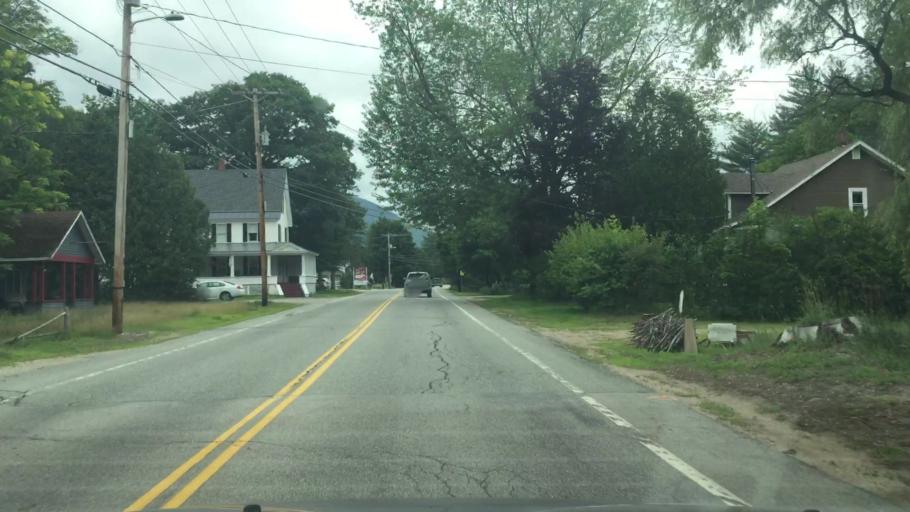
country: US
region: New Hampshire
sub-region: Carroll County
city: North Conway
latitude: 44.0782
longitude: -71.2749
